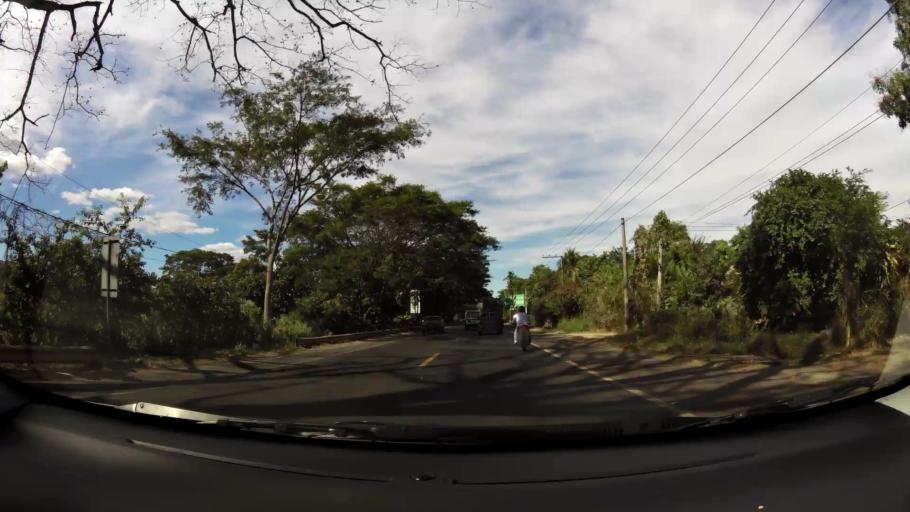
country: SV
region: San Salvador
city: Aguilares
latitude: 13.9258
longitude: -89.1853
